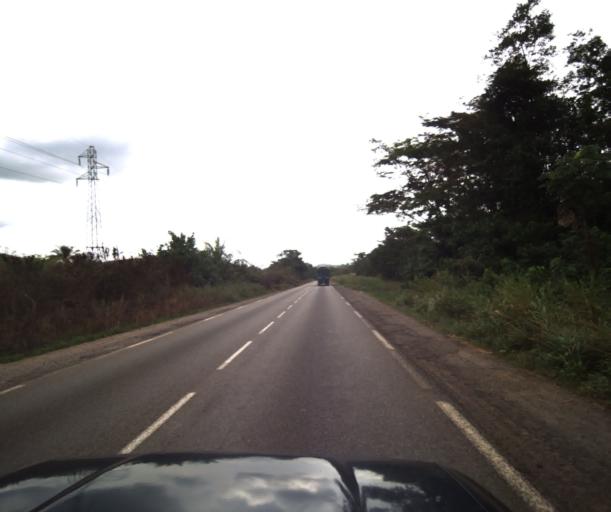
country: CM
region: Littoral
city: Edea
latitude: 3.8163
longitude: 10.3415
